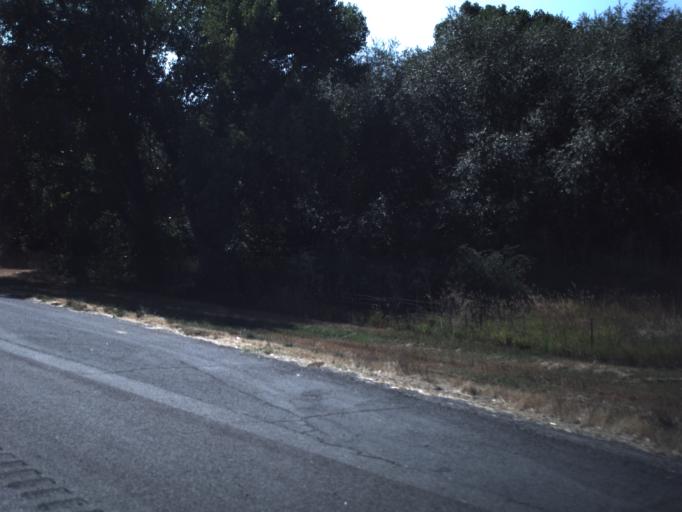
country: US
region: Utah
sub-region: Cache County
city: Wellsville
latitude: 41.6427
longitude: -111.9158
